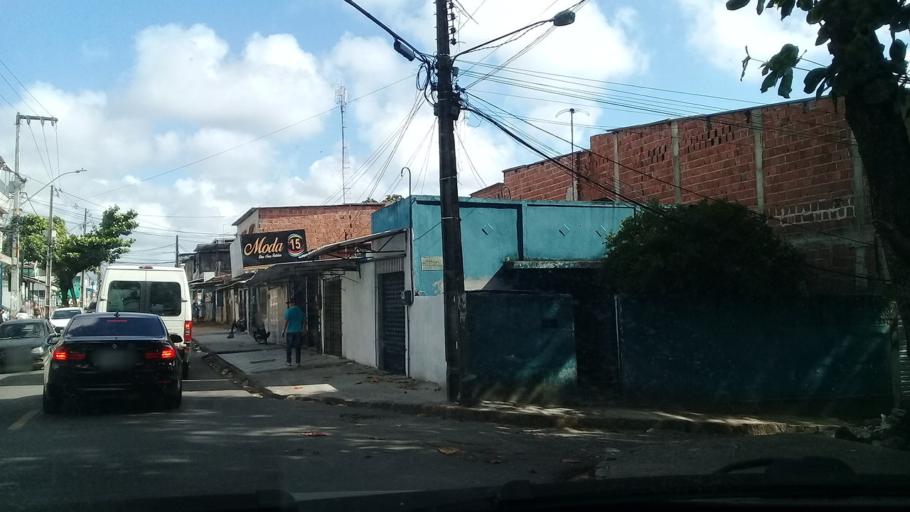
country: BR
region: Pernambuco
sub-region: Jaboatao Dos Guararapes
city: Jaboatao dos Guararapes
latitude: -8.1183
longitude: -34.9464
